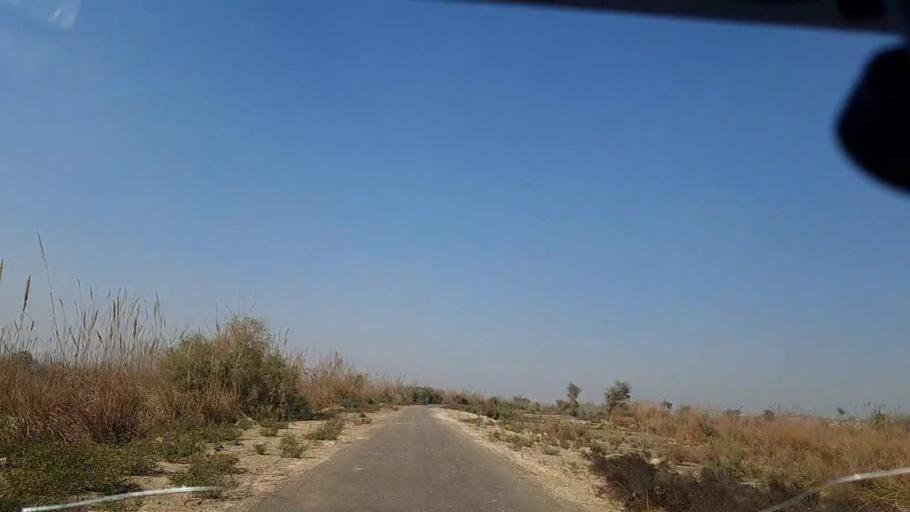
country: PK
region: Sindh
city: Khanpur
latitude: 27.5781
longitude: 69.3783
